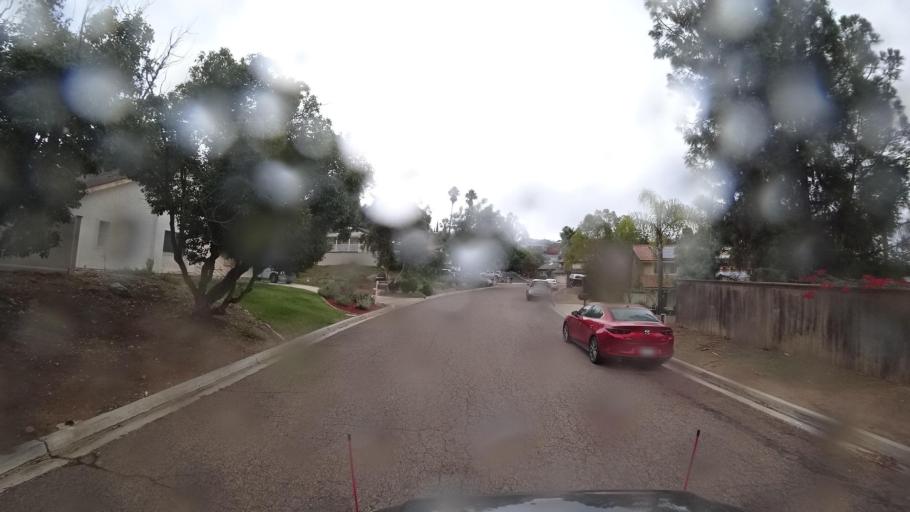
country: US
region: California
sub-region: San Diego County
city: Rancho San Diego
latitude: 32.7726
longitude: -116.9259
